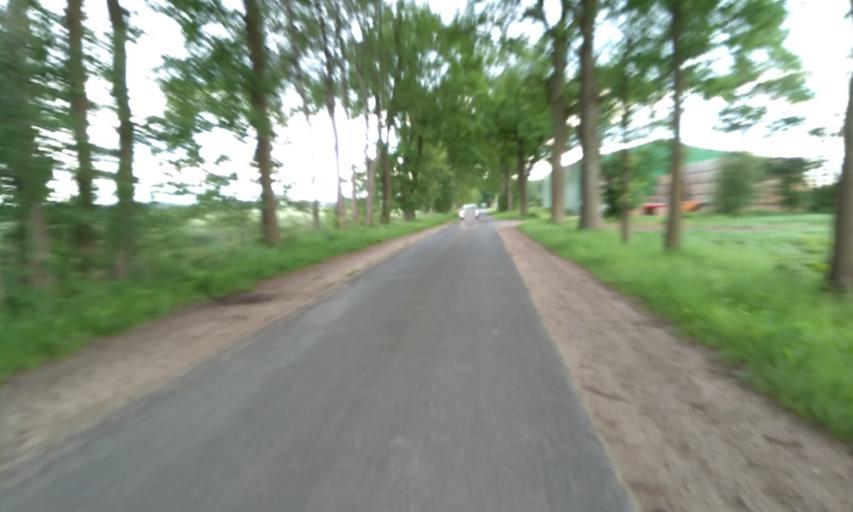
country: DE
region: Lower Saxony
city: Regesbostel
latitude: 53.3827
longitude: 9.6386
